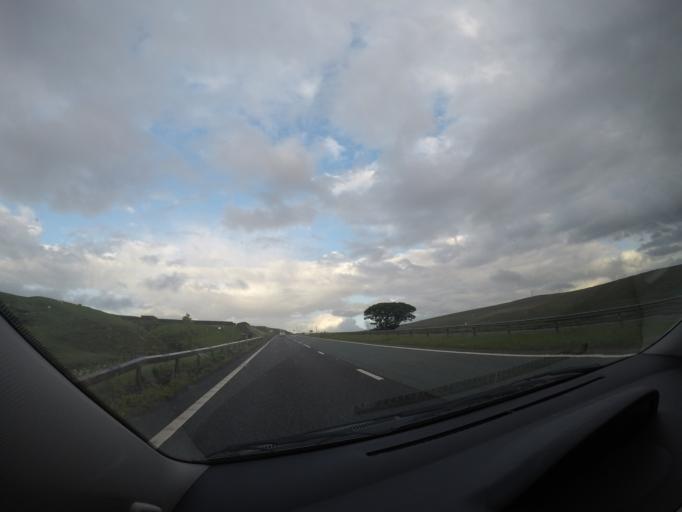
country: GB
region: England
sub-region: County Durham
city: Holwick
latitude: 54.5168
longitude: -2.2093
